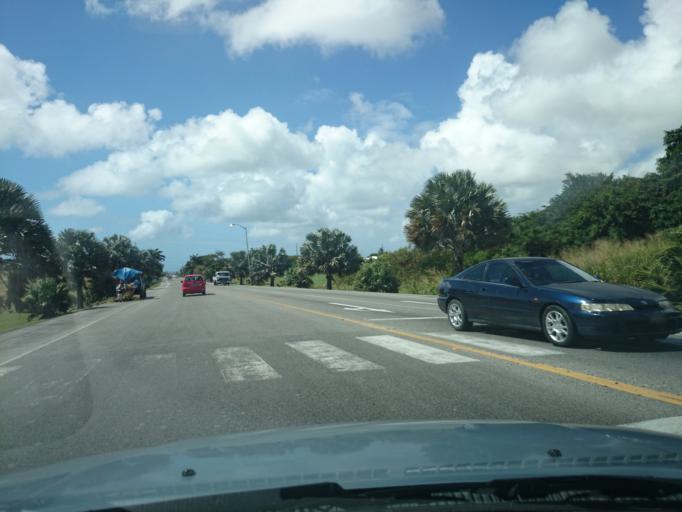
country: BB
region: Christ Church
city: Oistins
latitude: 13.0784
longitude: -59.5581
